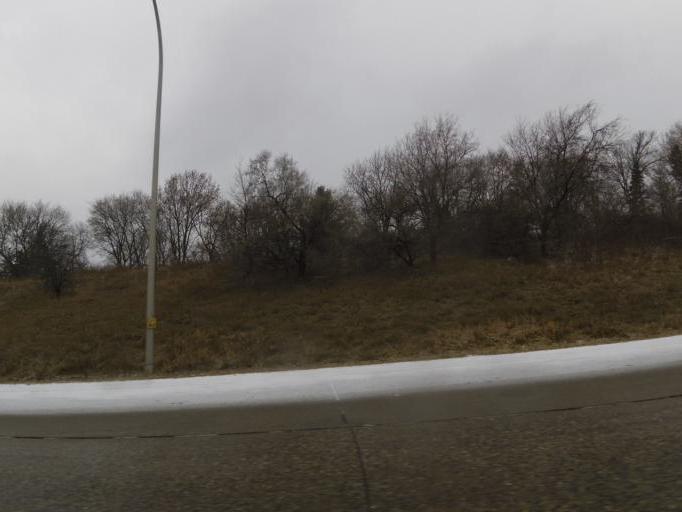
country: US
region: Minnesota
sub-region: Dakota County
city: Eagan
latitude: 44.8002
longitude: -93.2222
